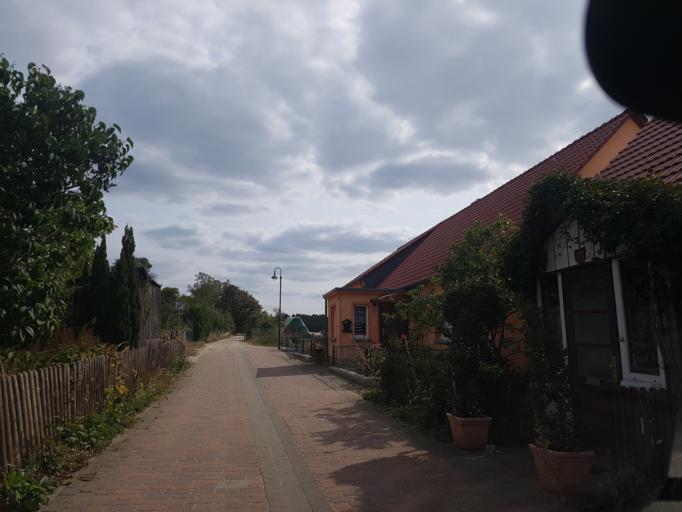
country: DE
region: Brandenburg
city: Wiesenburg
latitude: 52.1069
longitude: 12.3961
